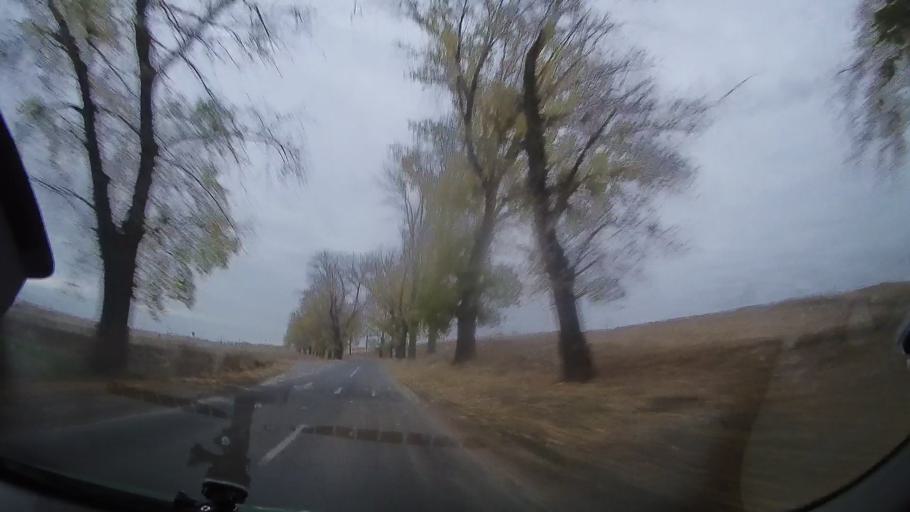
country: RO
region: Tulcea
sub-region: Comuna Mihai Bravu
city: Mihai Bravu
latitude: 44.9615
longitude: 28.6409
